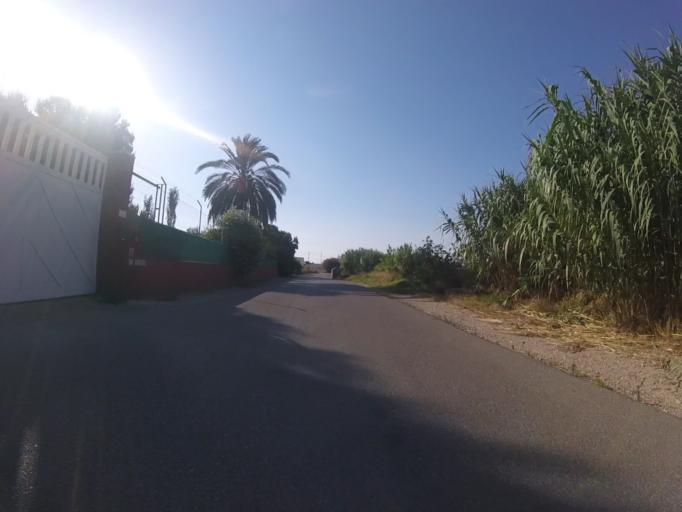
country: ES
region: Valencia
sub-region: Provincia de Castello
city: Benicarlo
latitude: 40.4237
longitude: 0.4339
